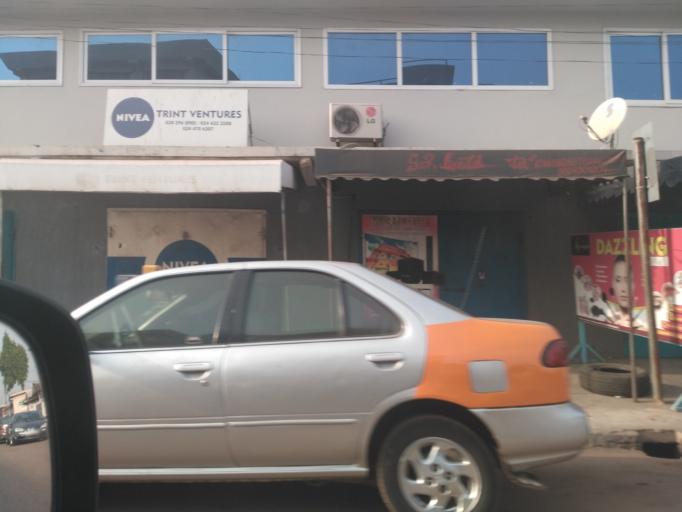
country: GH
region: Greater Accra
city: Accra
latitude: 5.5963
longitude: -0.1945
